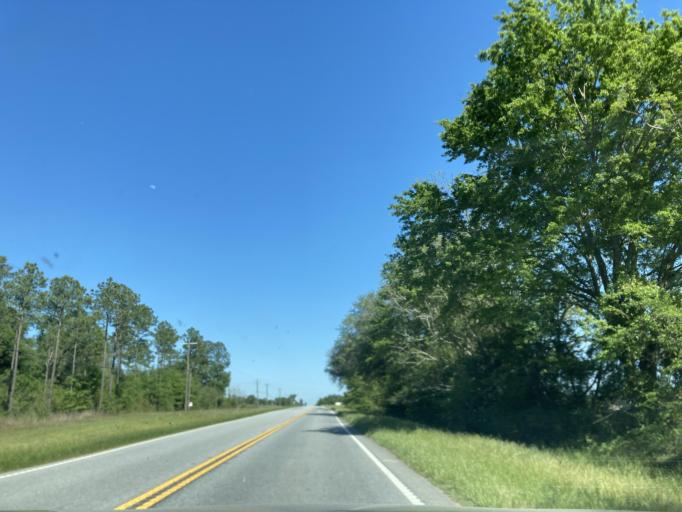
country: US
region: Georgia
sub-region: Miller County
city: Colquitt
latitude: 31.1858
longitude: -84.6173
